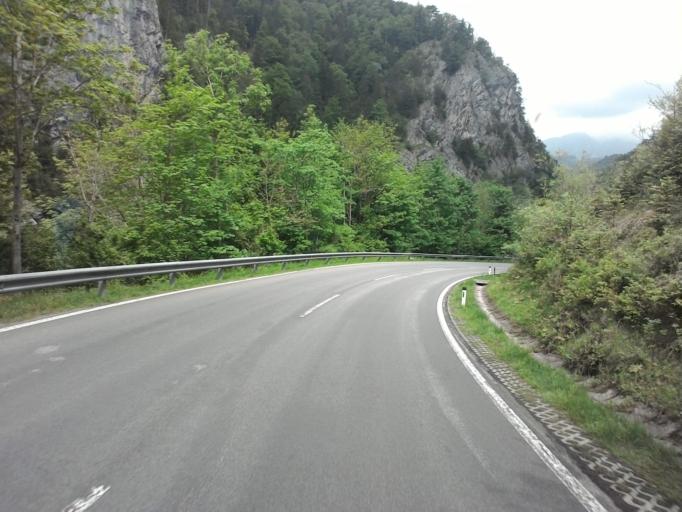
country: AT
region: Styria
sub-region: Politischer Bezirk Leoben
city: Hieflau
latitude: 47.6259
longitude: 14.7559
